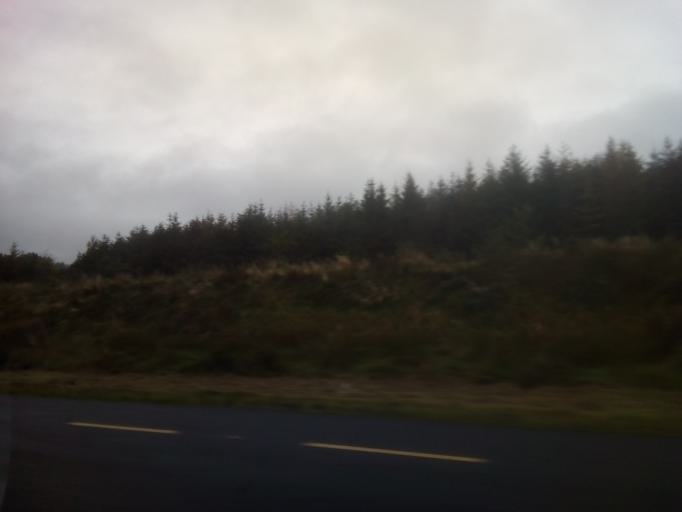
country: IE
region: Connaught
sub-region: Roscommon
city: Ballaghaderreen
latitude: 53.9006
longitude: -8.5365
